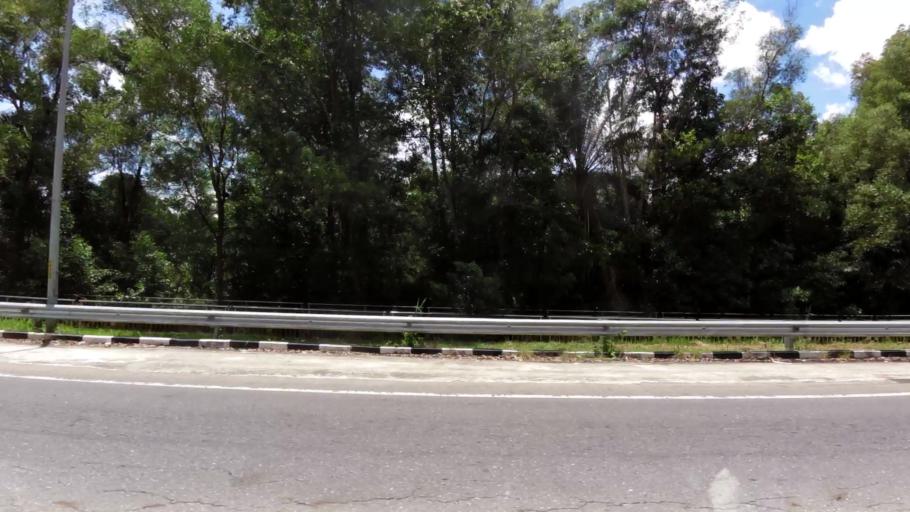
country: BN
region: Brunei and Muara
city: Bandar Seri Begawan
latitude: 4.9573
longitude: 114.9176
